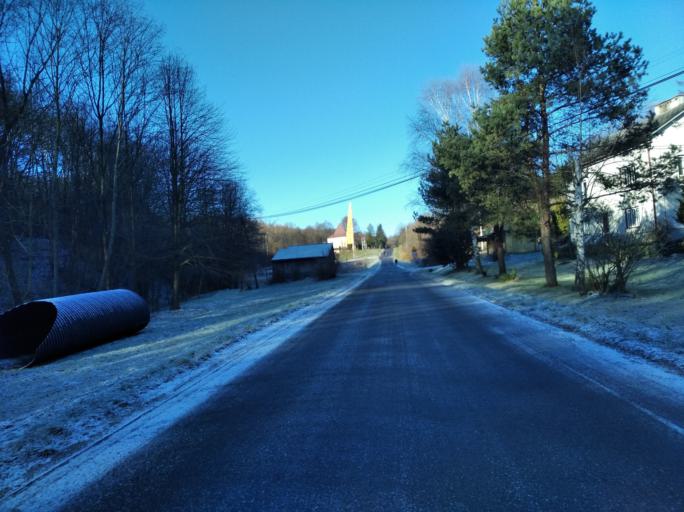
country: PL
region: Subcarpathian Voivodeship
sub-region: Powiat strzyzowski
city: Czudec
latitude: 49.9536
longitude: 21.7703
